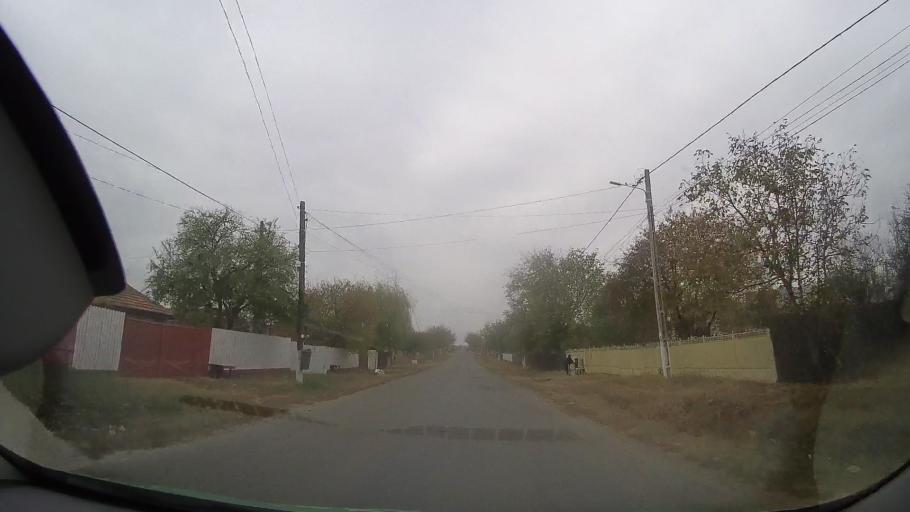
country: RO
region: Buzau
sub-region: Comuna Luciu
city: Luciu
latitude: 44.9739
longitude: 27.0707
